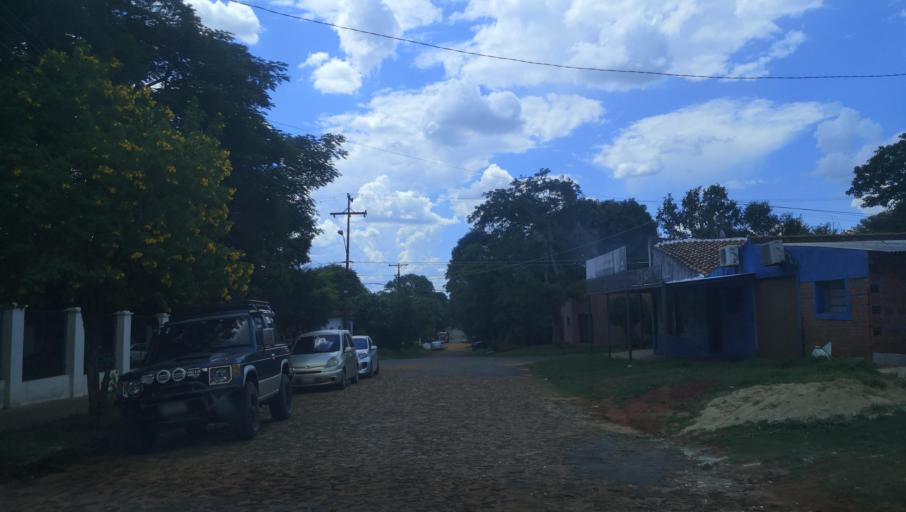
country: PY
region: Misiones
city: Santa Maria
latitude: -26.8892
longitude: -57.0322
